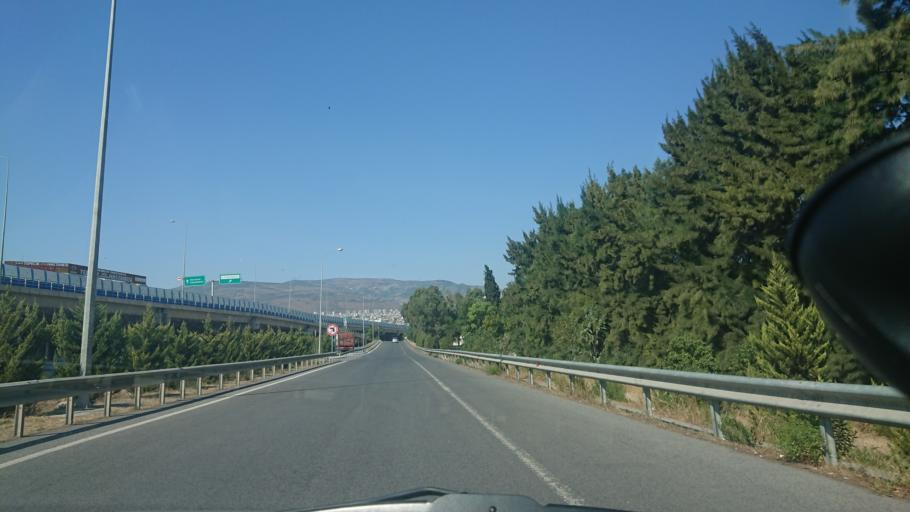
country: TR
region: Izmir
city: Bornova
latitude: 38.4526
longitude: 27.2064
